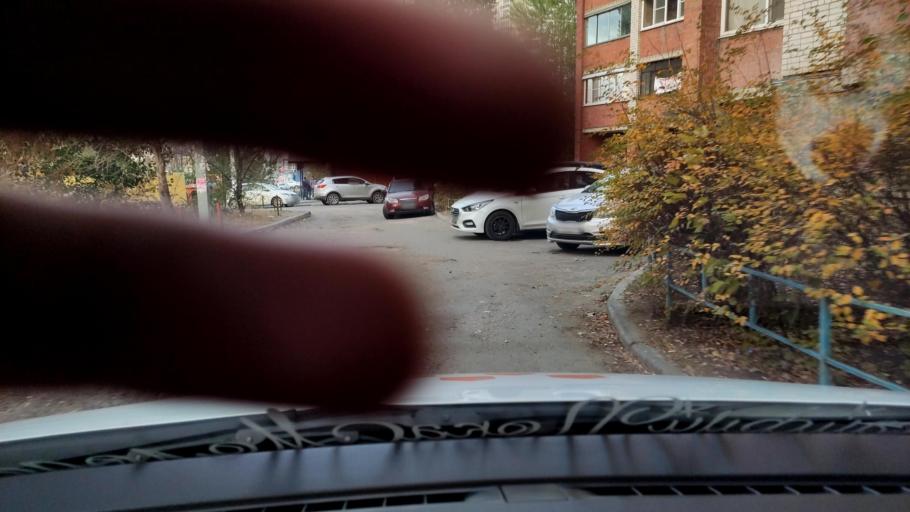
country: RU
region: Voronezj
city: Podgornoye
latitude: 51.7112
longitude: 39.1447
